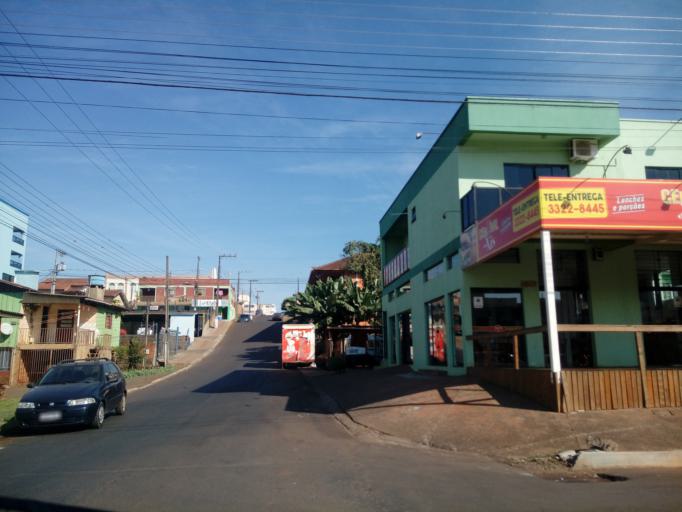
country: BR
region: Santa Catarina
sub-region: Chapeco
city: Chapeco
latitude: -27.0947
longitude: -52.6732
